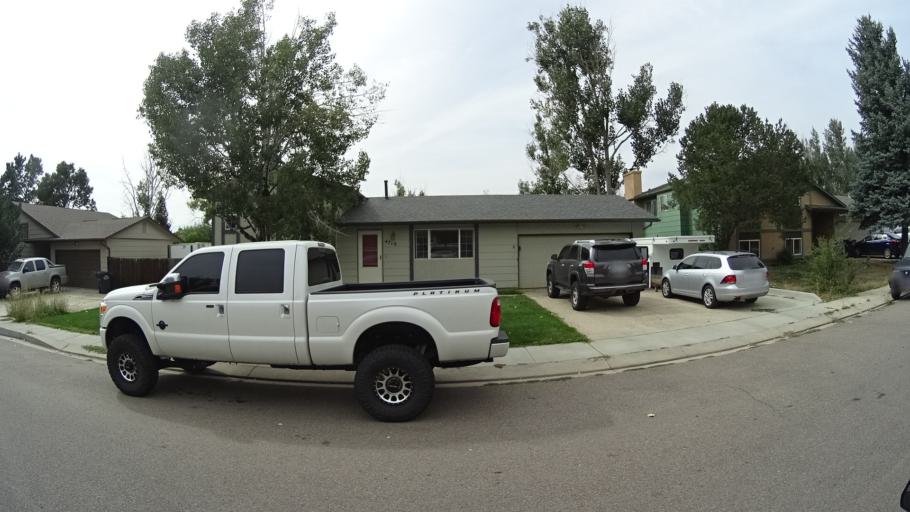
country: US
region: Colorado
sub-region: El Paso County
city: Cimarron Hills
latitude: 38.9002
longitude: -104.7378
